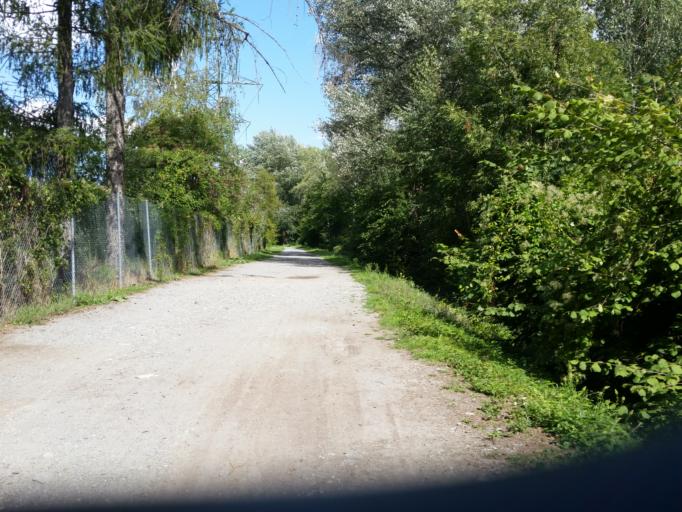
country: CH
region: Valais
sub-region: Conthey District
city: Basse-Nendaz
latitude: 46.2104
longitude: 7.3293
